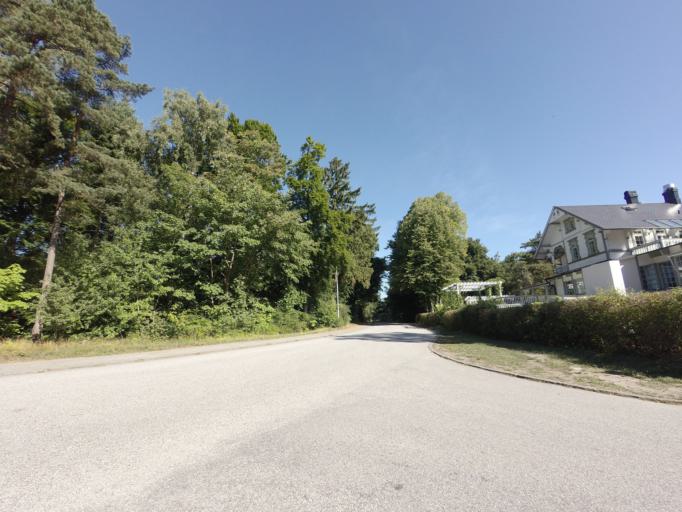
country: SE
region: Skane
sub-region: Ystads Kommun
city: Ystad
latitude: 55.4269
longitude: 13.8495
